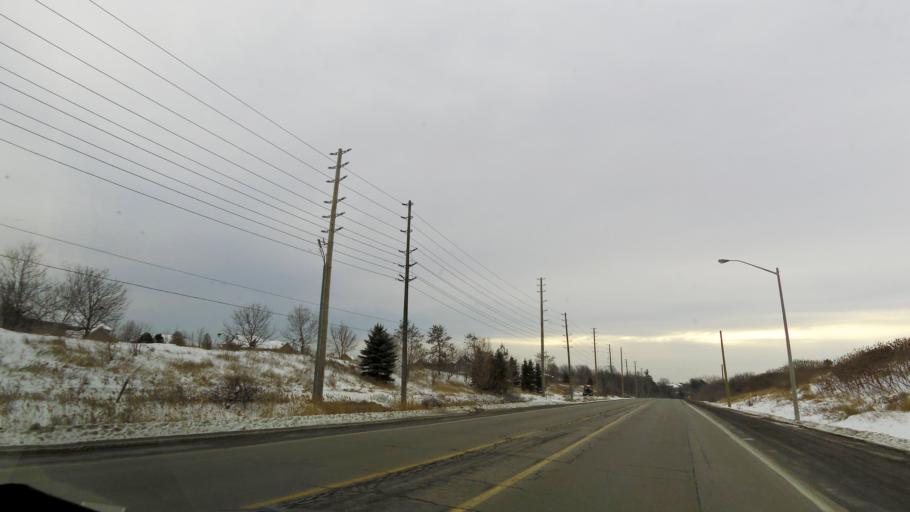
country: CA
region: Ontario
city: Vaughan
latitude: 43.8298
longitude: -79.6217
